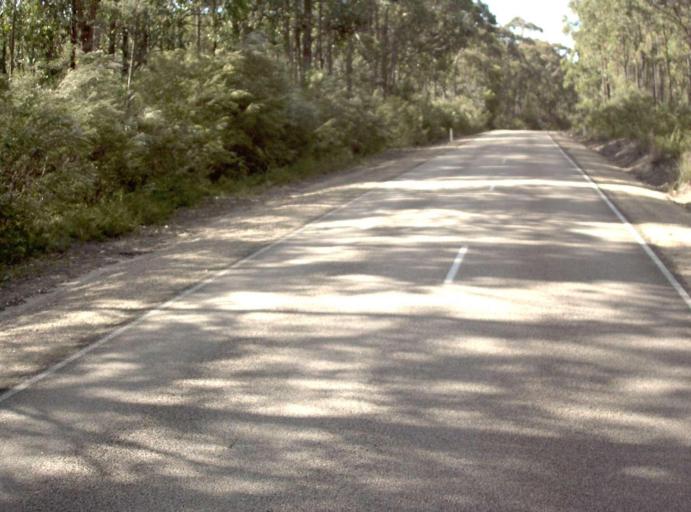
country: AU
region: Victoria
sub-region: East Gippsland
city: Lakes Entrance
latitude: -37.6361
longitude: 148.1105
